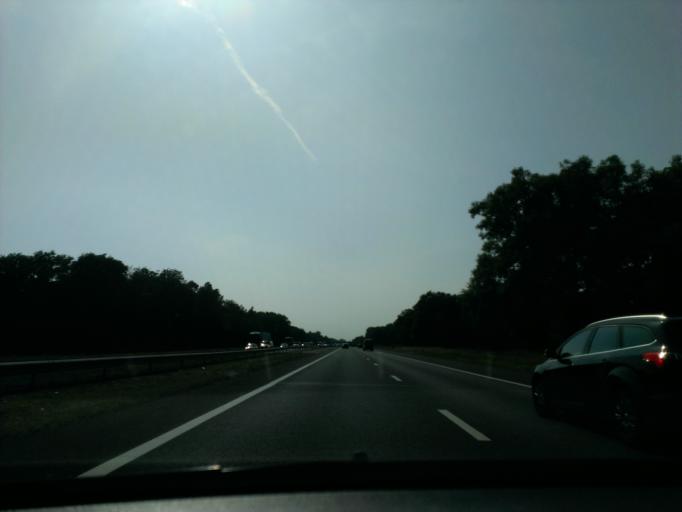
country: NL
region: Overijssel
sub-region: Gemeente Hof van Twente
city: Goor
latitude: 52.2901
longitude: 6.6242
